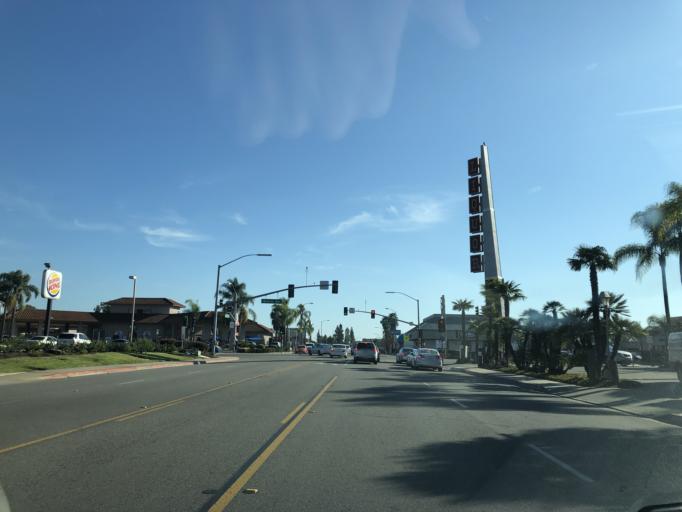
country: US
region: California
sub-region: San Diego County
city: Escondido
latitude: 33.1297
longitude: -117.0898
